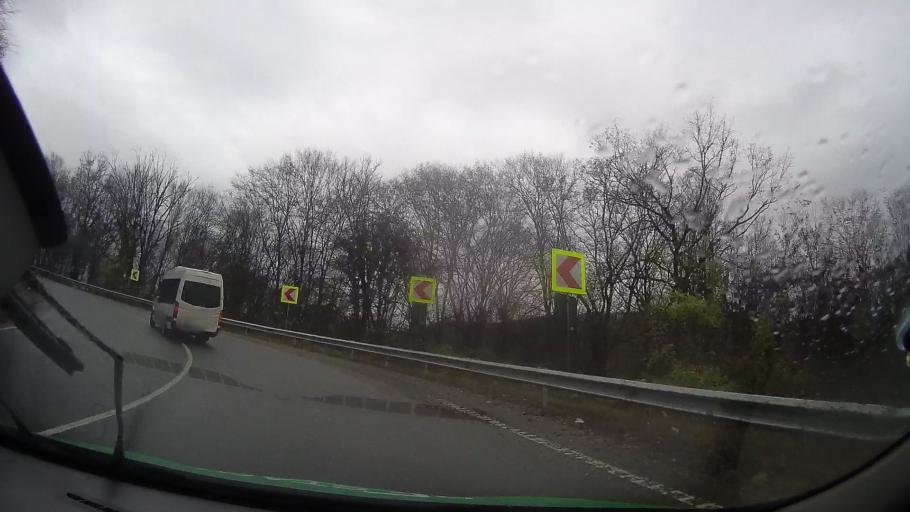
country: RO
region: Bistrita-Nasaud
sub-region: Comuna Sieu-Magherus
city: Sieu-Magherus
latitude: 47.0417
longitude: 24.4203
